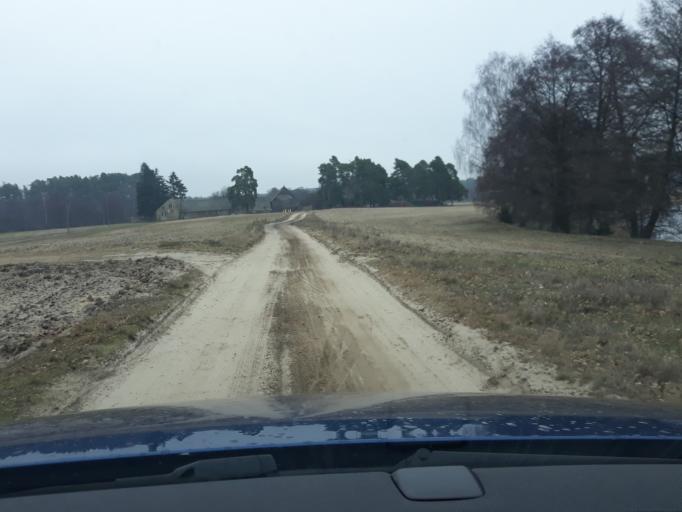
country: PL
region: Pomeranian Voivodeship
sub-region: Powiat chojnicki
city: Brusy
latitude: 53.8635
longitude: 17.5559
